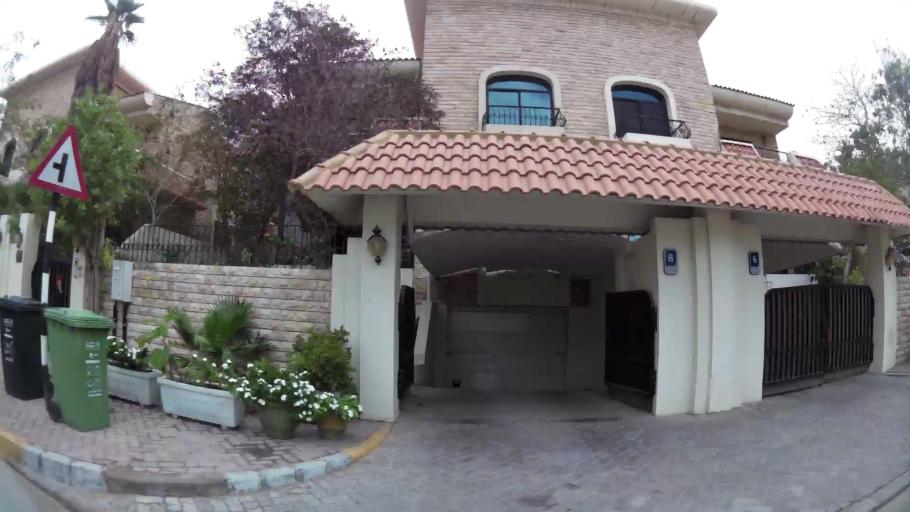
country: AE
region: Abu Dhabi
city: Abu Dhabi
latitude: 24.4655
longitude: 54.3358
